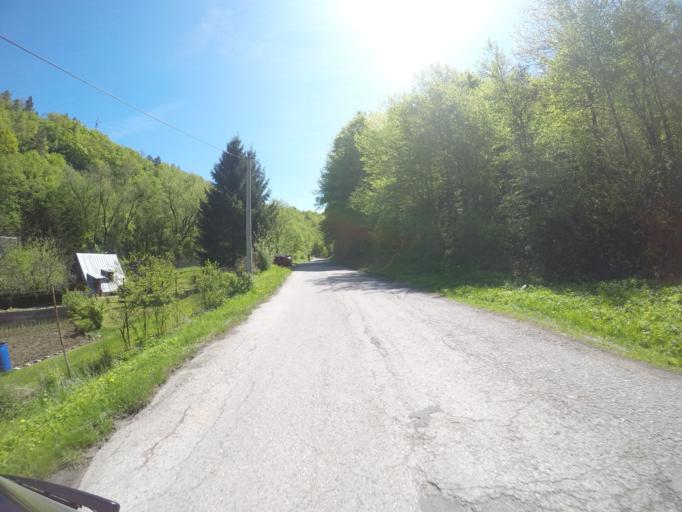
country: SK
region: Banskobystricky
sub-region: Okres Banska Bystrica
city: Banska Bystrica
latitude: 48.7247
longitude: 19.2146
